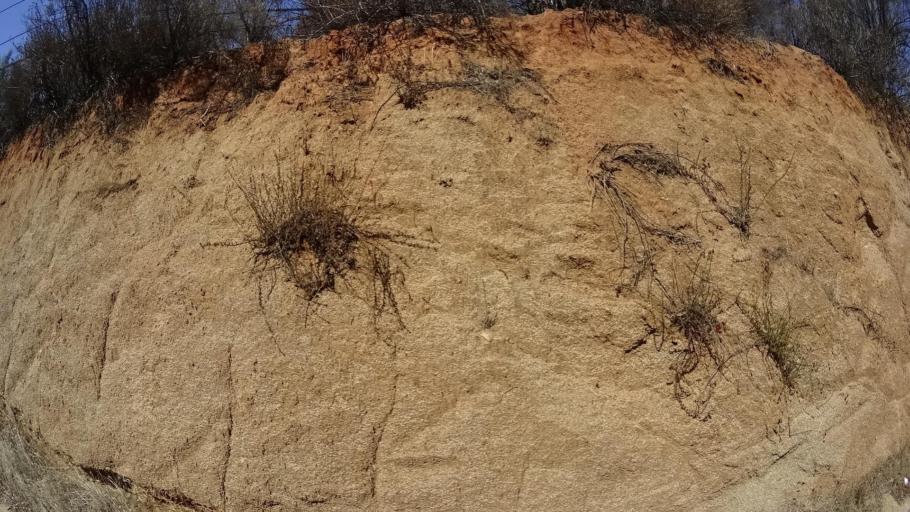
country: US
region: California
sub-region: San Diego County
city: Valley Center
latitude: 33.2344
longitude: -117.0329
